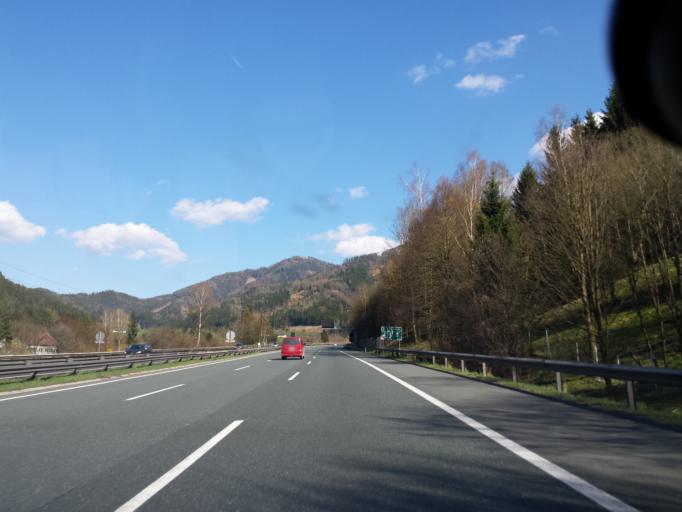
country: AT
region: Styria
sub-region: Politischer Bezirk Leoben
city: Sankt Michael in Obersteiermark
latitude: 47.3192
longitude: 15.0406
